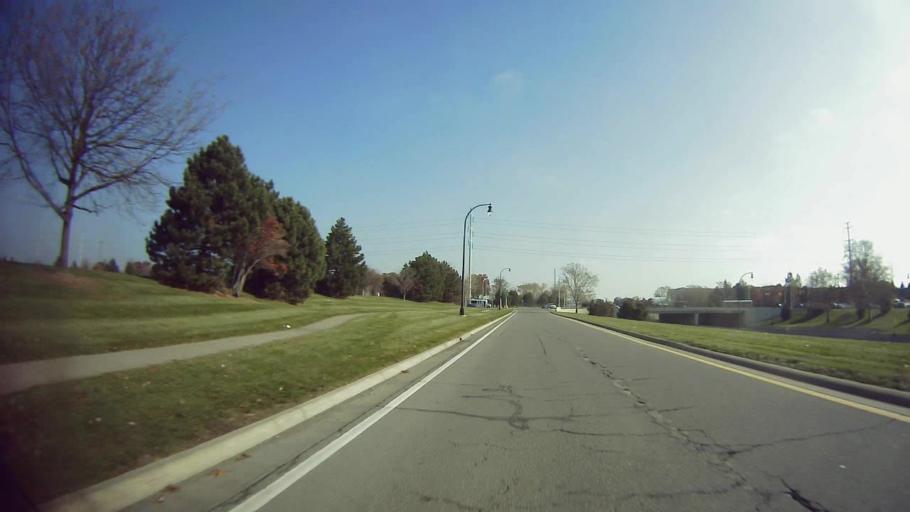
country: US
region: Michigan
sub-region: Wayne County
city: Dearborn
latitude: 42.3297
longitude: -83.1953
